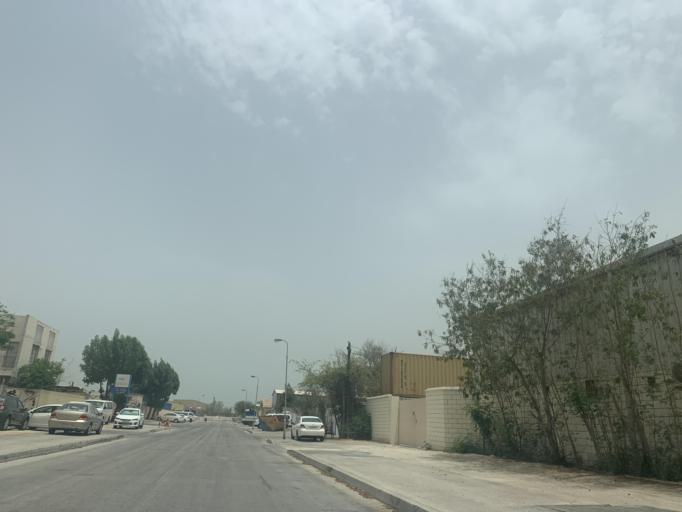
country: BH
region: Northern
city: Sitrah
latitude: 26.1785
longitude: 50.6069
